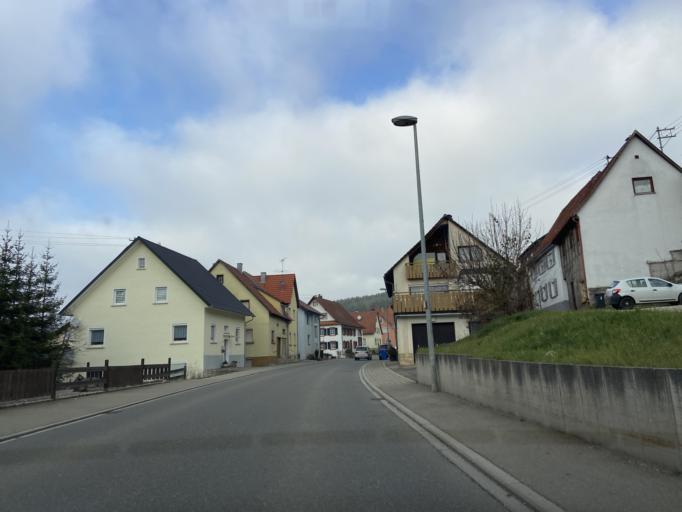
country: DE
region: Baden-Wuerttemberg
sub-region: Tuebingen Region
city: Neufra
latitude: 48.2483
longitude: 9.1829
